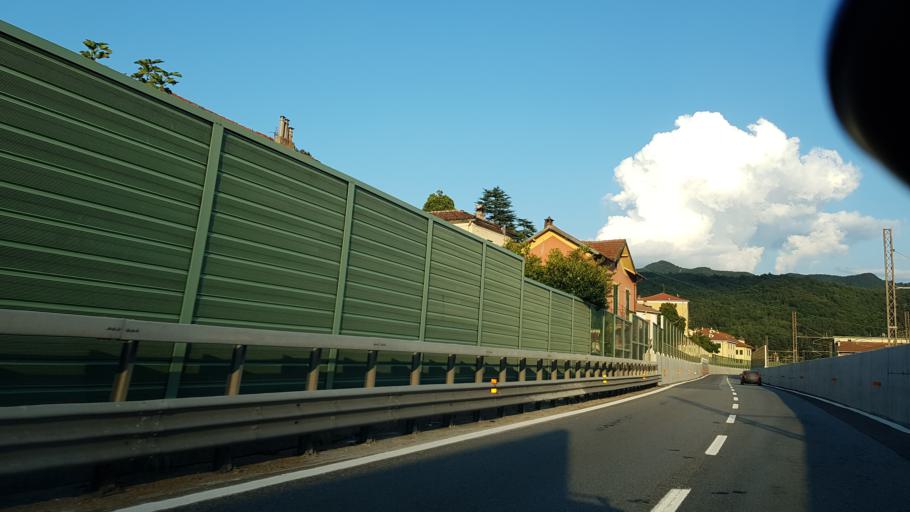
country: IT
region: Liguria
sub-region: Provincia di Genova
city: Ronco Scrivia
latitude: 44.6155
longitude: 8.9500
